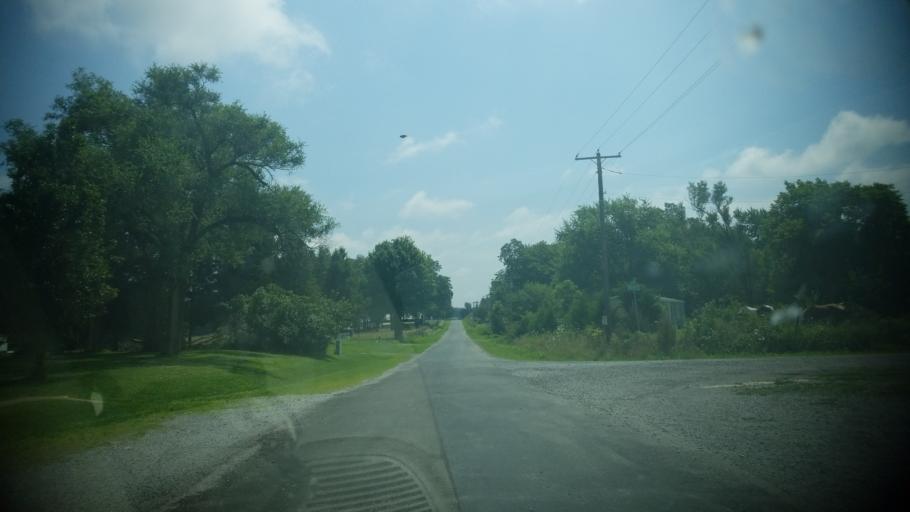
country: US
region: Illinois
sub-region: Wayne County
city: Fairfield
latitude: 38.5224
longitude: -88.3579
